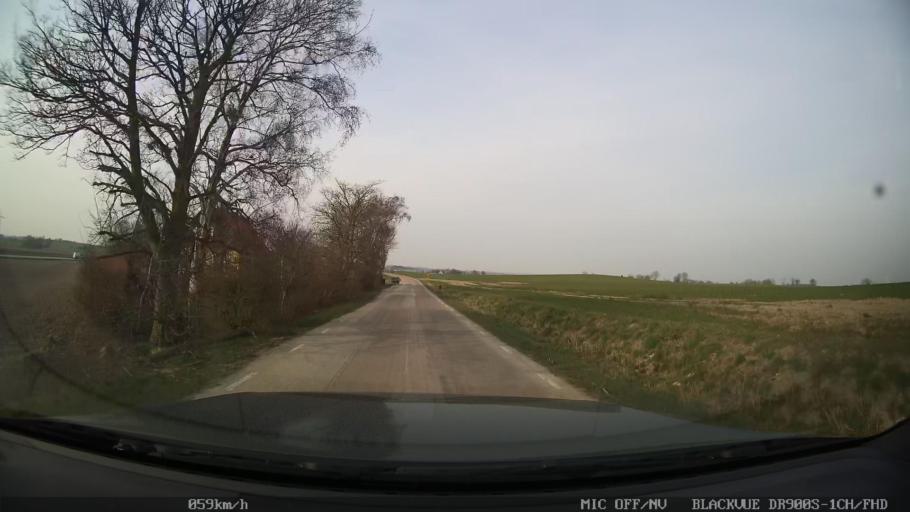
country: SE
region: Skane
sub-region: Ystads Kommun
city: Ystad
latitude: 55.4734
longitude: 13.8006
